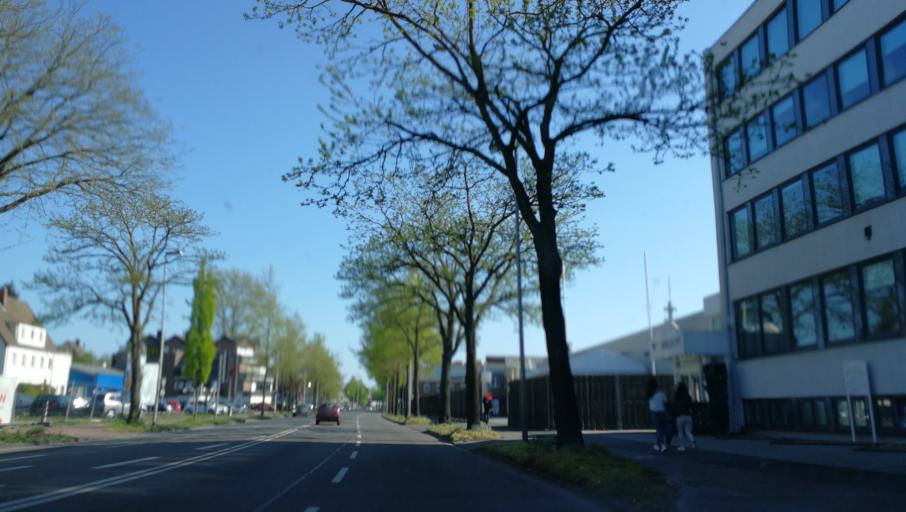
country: DE
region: North Rhine-Westphalia
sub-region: Regierungsbezirk Munster
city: Rheine
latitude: 52.2752
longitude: 7.4390
